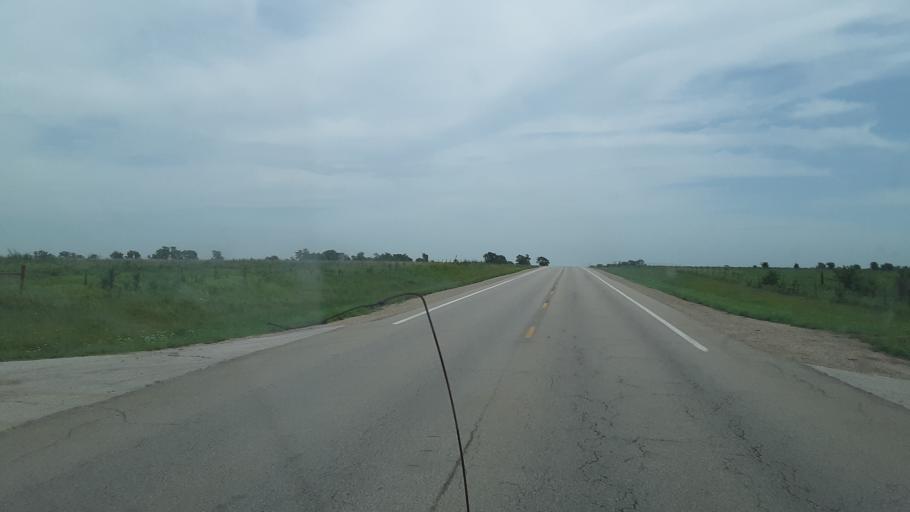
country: US
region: Kansas
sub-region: Woodson County
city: Yates Center
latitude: 37.8363
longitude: -95.9039
